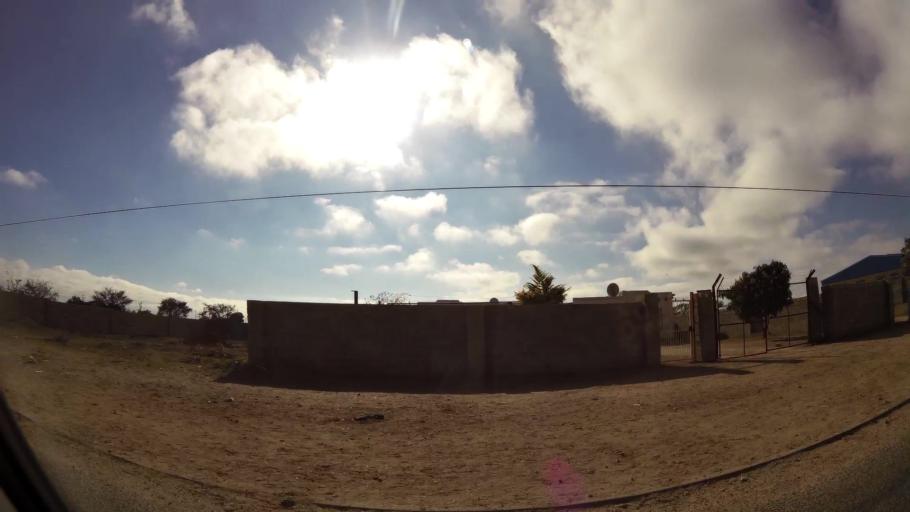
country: ZA
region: Limpopo
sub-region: Capricorn District Municipality
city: Polokwane
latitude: -23.8507
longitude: 29.3820
